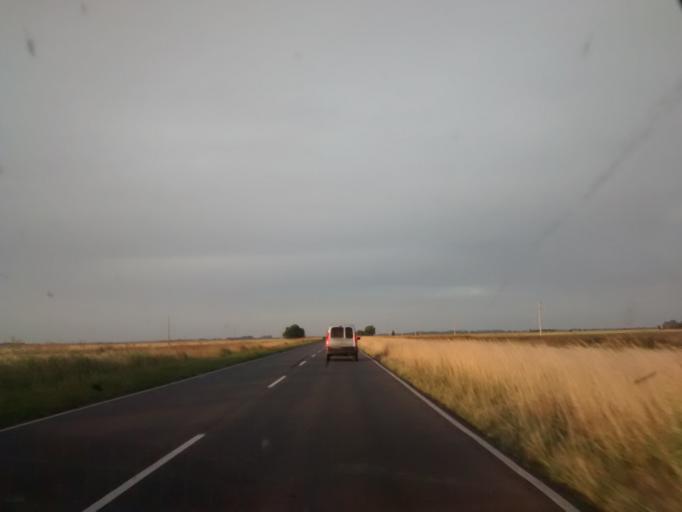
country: AR
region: Buenos Aires
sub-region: Partido de General Belgrano
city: General Belgrano
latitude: -35.9457
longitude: -58.6203
